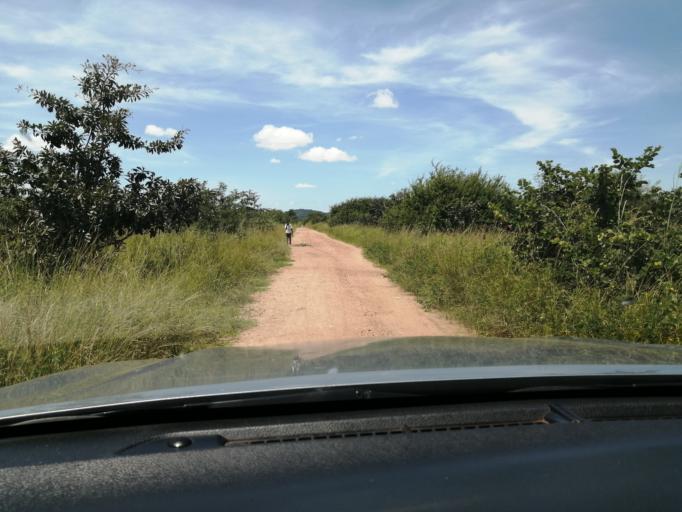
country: ZM
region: Central
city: Chibombo
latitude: -15.0633
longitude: 27.8307
